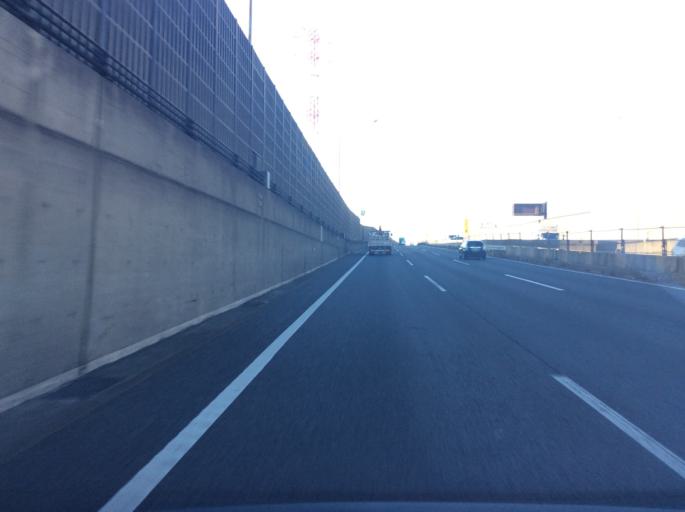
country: JP
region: Chiba
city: Nagareyama
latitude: 35.8497
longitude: 139.8751
